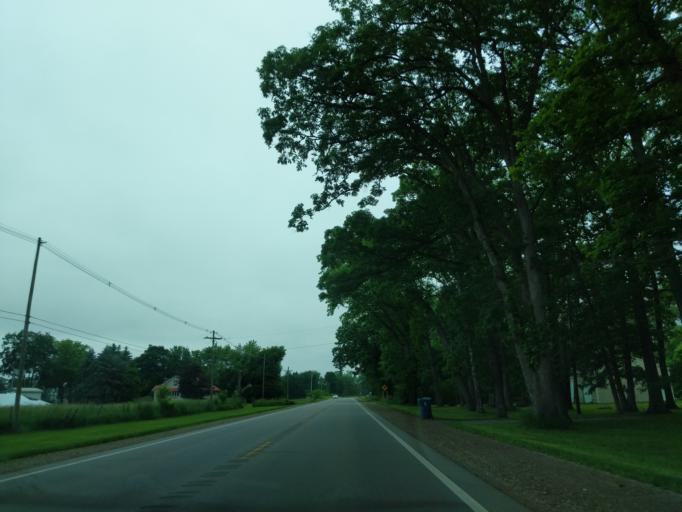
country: US
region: Michigan
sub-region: Branch County
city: Quincy
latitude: 41.9495
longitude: -84.8074
